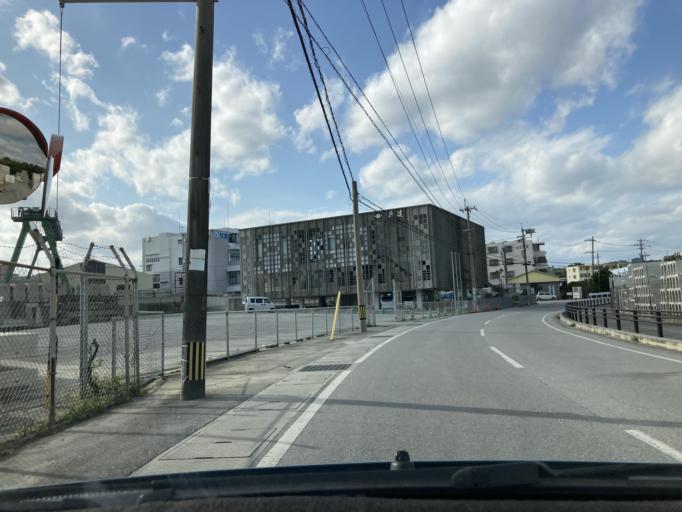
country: JP
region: Okinawa
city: Tomigusuku
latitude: 26.1938
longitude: 127.7491
